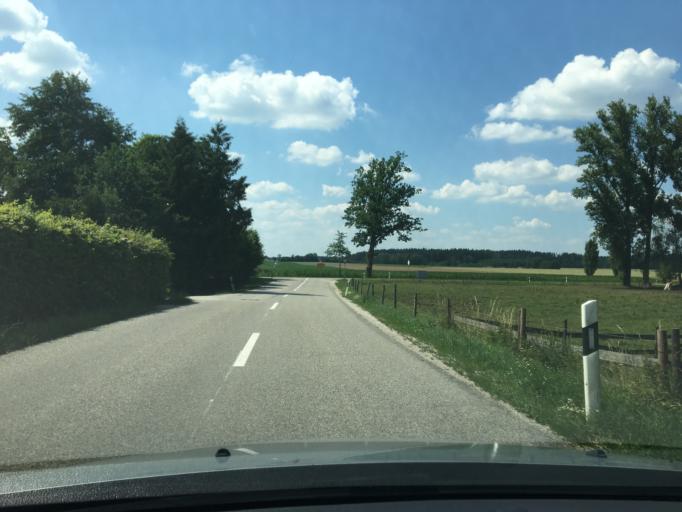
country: DE
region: Bavaria
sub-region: Lower Bavaria
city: Vilsbiburg
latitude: 48.4317
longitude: 12.3447
